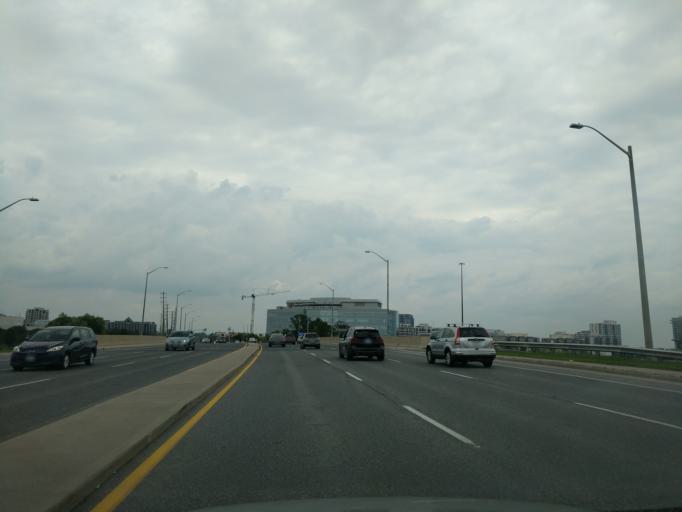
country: CA
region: Ontario
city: Markham
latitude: 43.8442
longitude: -79.3306
